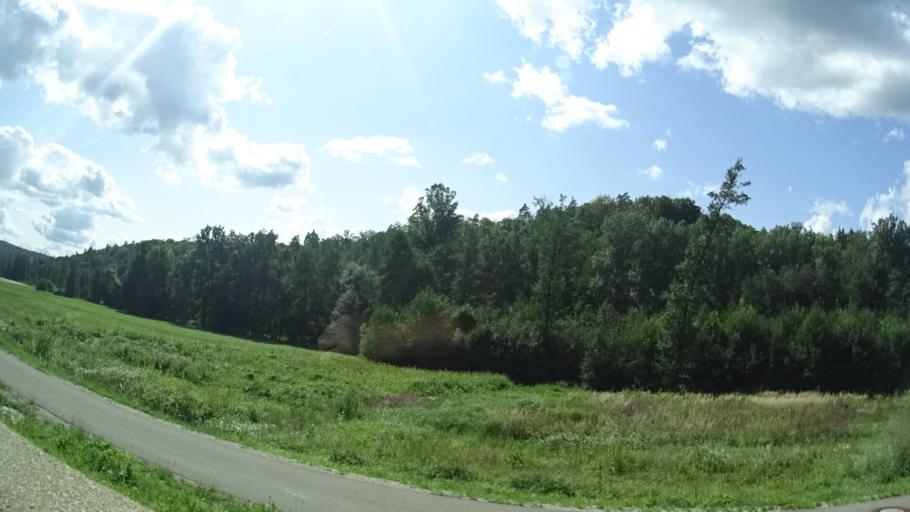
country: DE
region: Bavaria
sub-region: Regierungsbezirk Unterfranken
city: Breitbrunn
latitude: 50.0016
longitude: 10.6908
